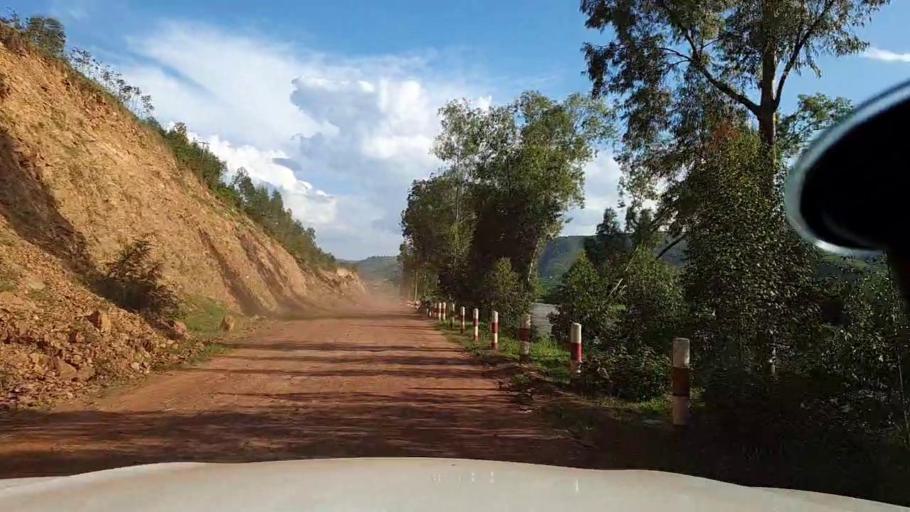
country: RW
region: Kigali
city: Kigali
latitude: -1.8711
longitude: 29.9320
